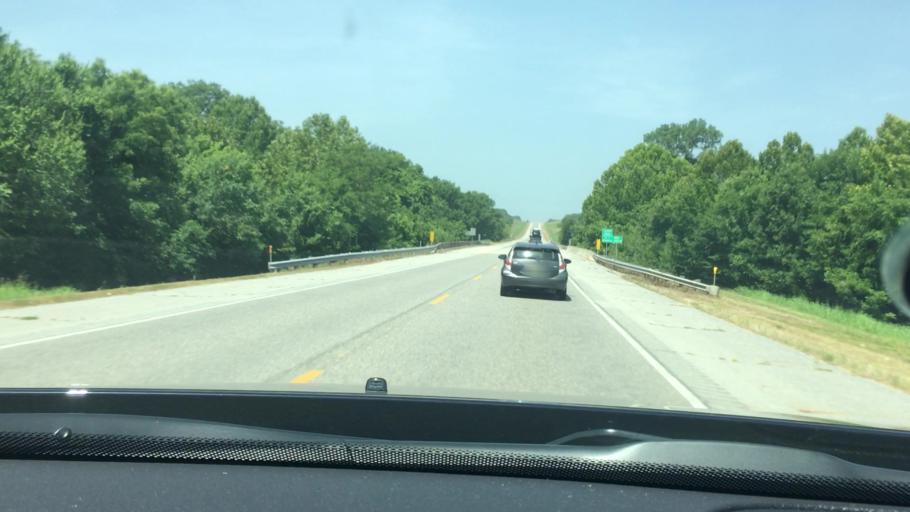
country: US
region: Oklahoma
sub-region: Coal County
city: Coalgate
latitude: 34.6110
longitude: -96.3926
